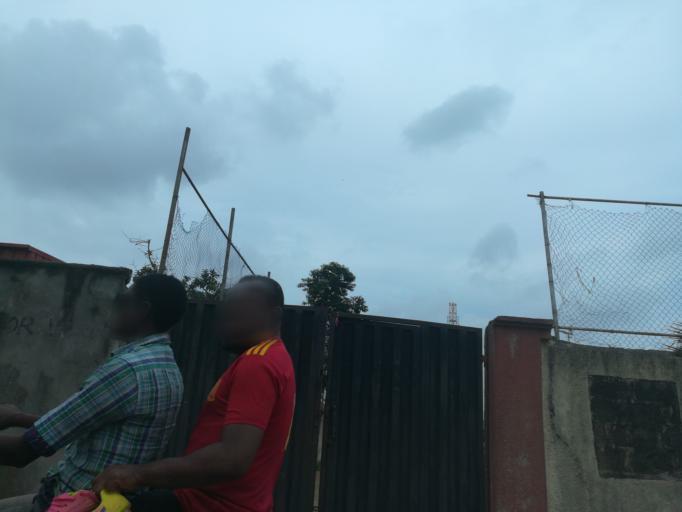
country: NG
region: Lagos
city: Oshodi
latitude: 6.5634
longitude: 3.3446
